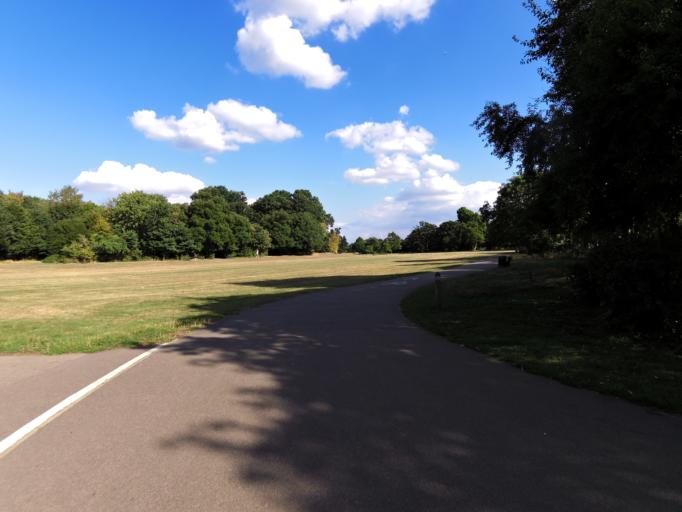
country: GB
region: England
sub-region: Greater London
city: Wood Green
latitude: 51.6195
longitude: -0.1332
